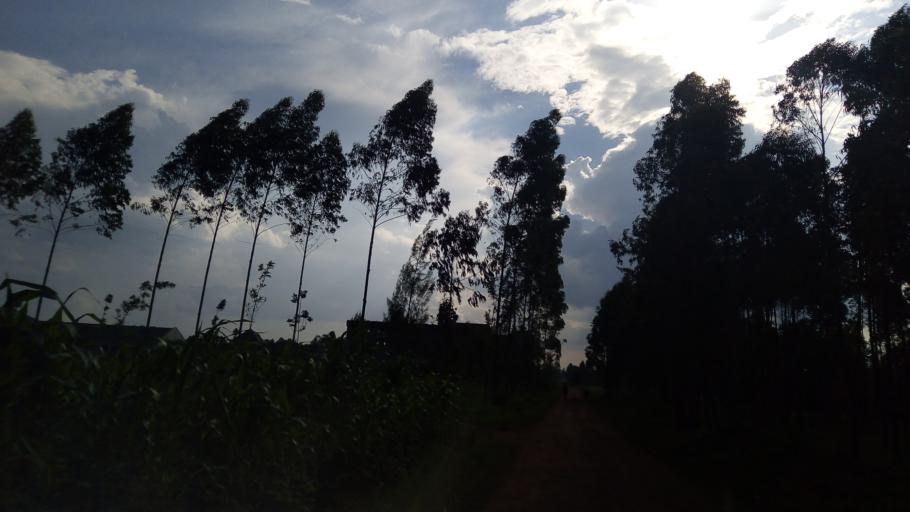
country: UG
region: Eastern Region
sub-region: Mbale District
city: Mbale
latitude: 1.0589
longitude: 34.1700
